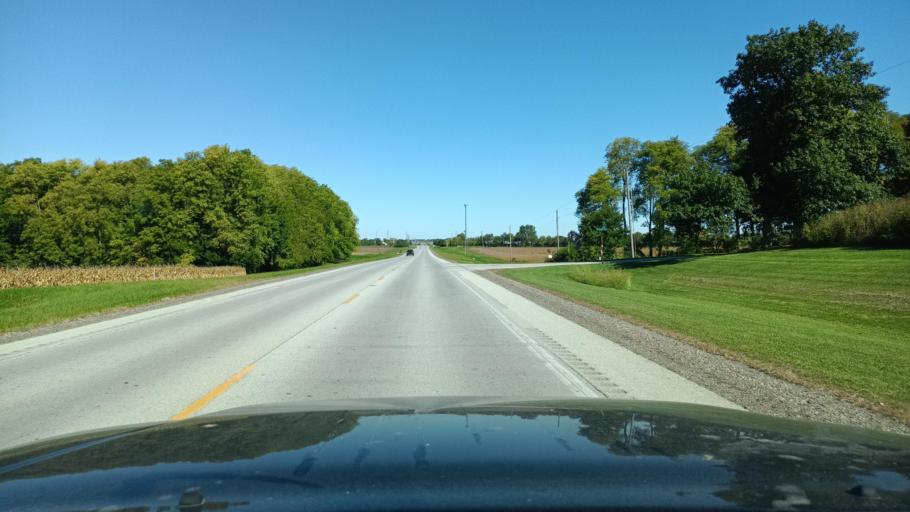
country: US
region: Illinois
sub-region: Champaign County
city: Urbana
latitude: 40.0757
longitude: -88.1620
